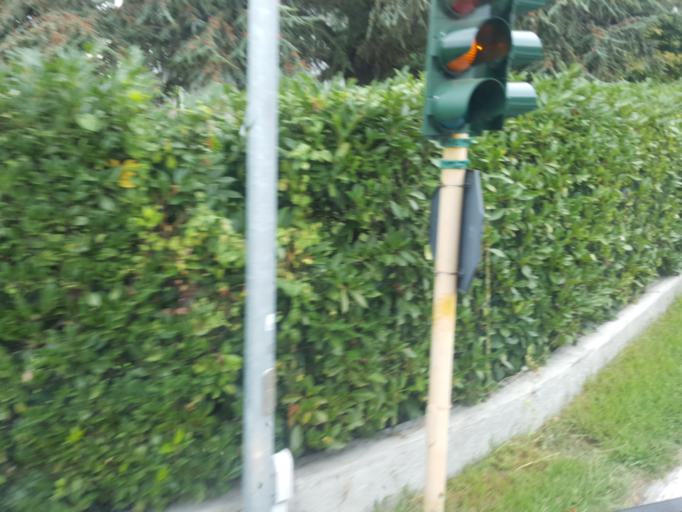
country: IT
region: Tuscany
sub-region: Provincia di Lucca
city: Forte dei Marmi
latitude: 43.9676
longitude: 10.1769
